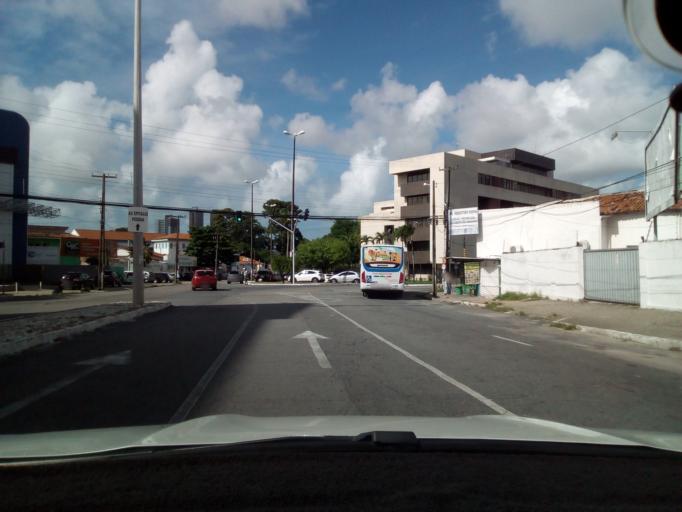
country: BR
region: Paraiba
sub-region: Joao Pessoa
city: Joao Pessoa
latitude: -7.1205
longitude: -34.8743
